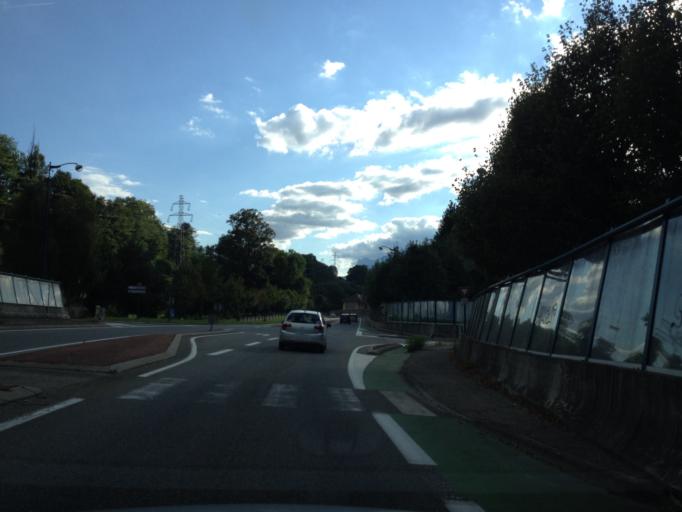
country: FR
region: Rhone-Alpes
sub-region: Departement de l'Isere
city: Pontcharra
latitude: 45.4325
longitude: 6.0270
